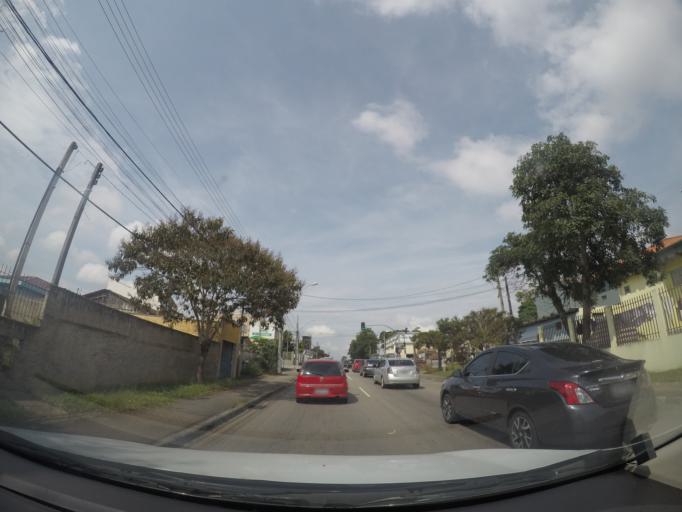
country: BR
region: Parana
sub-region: Curitiba
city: Curitiba
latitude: -25.4909
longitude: -49.2884
